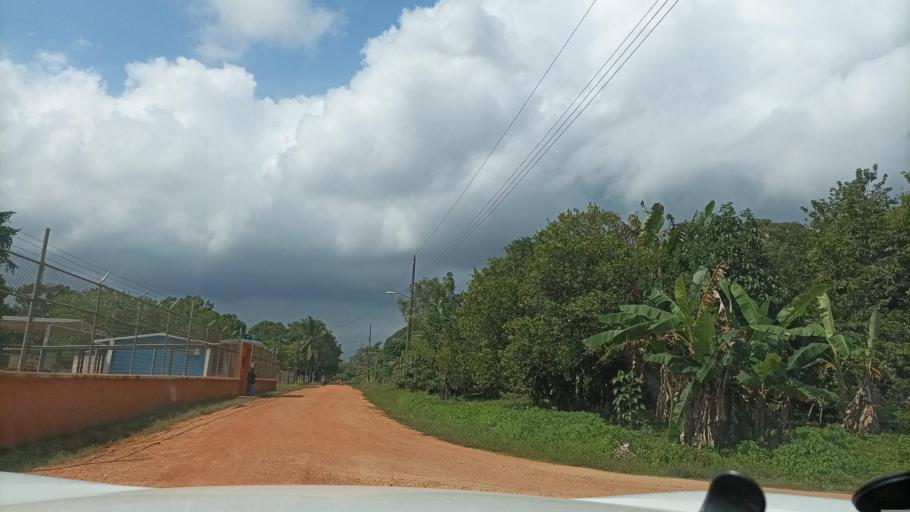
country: MX
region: Veracruz
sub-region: Chinameca
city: Chacalapa
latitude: 18.0804
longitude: -94.6703
